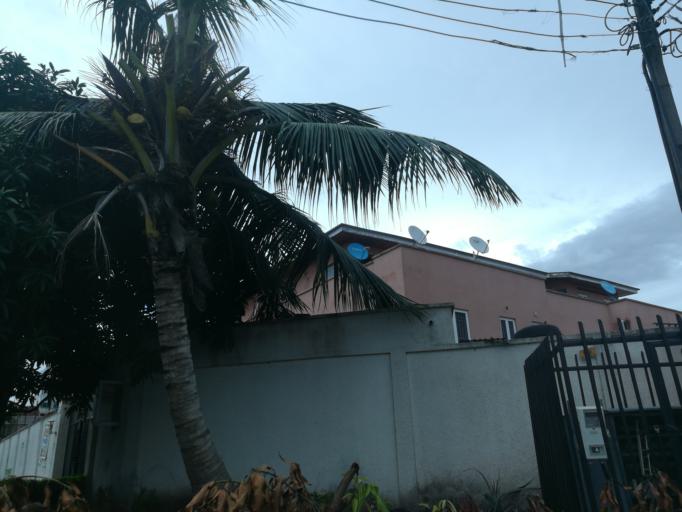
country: NG
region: Lagos
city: Ikoyi
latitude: 6.4459
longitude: 3.4739
